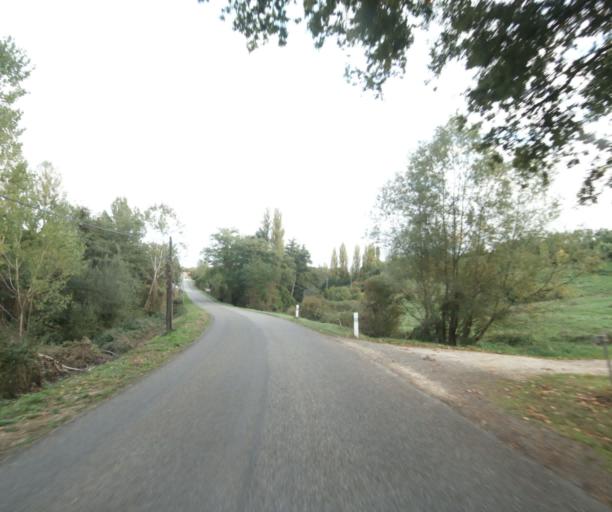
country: FR
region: Aquitaine
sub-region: Departement des Landes
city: Gabarret
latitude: 43.9496
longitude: 0.0796
